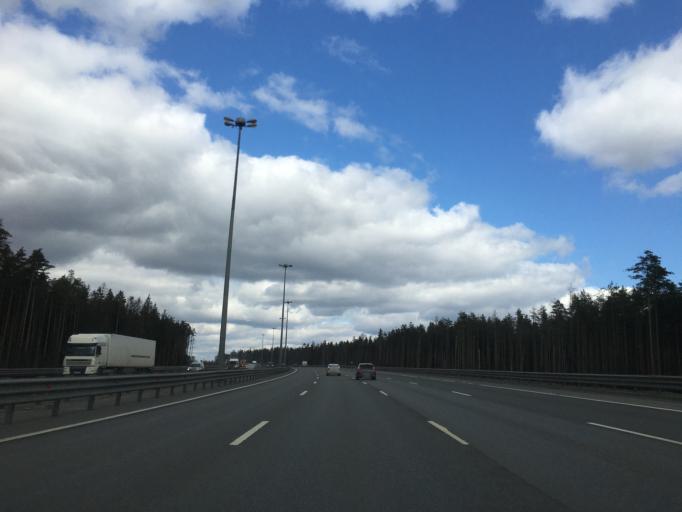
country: RU
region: Leningrad
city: Yanino Vtoroye
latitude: 59.9608
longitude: 30.5538
